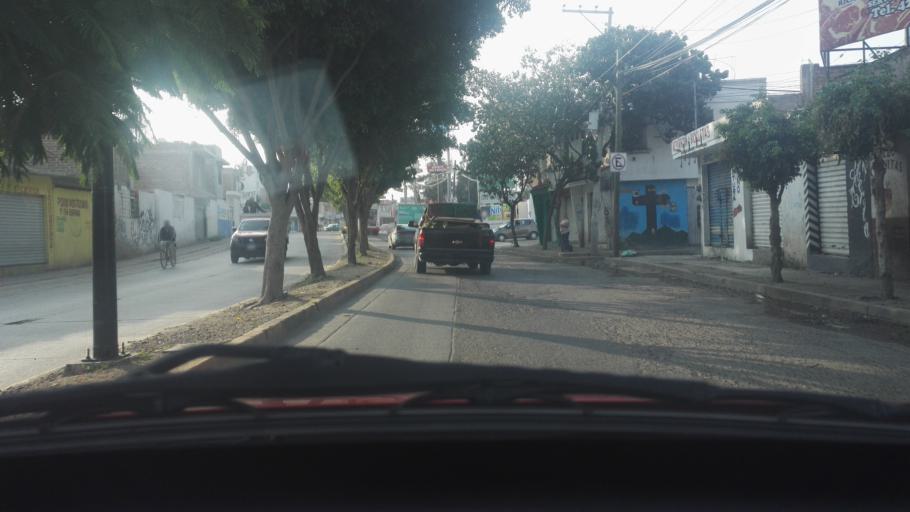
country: MX
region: Guanajuato
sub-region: Leon
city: Fraccionamiento Paraiso Real
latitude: 21.0977
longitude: -101.6049
